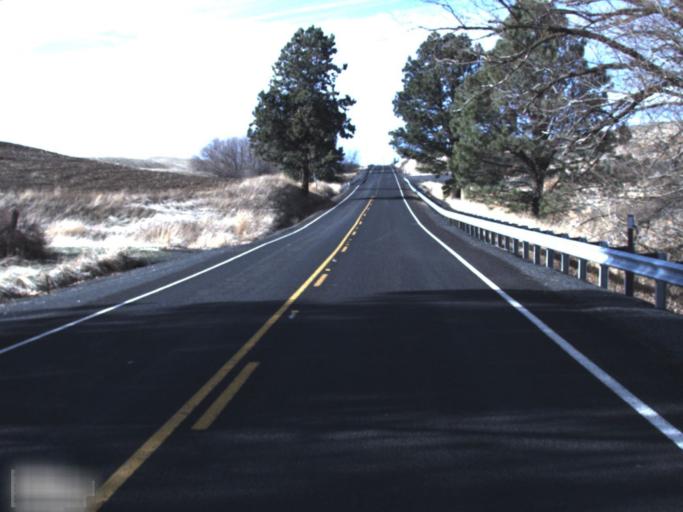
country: US
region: Washington
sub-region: Whitman County
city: Pullman
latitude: 46.9289
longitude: -117.1124
